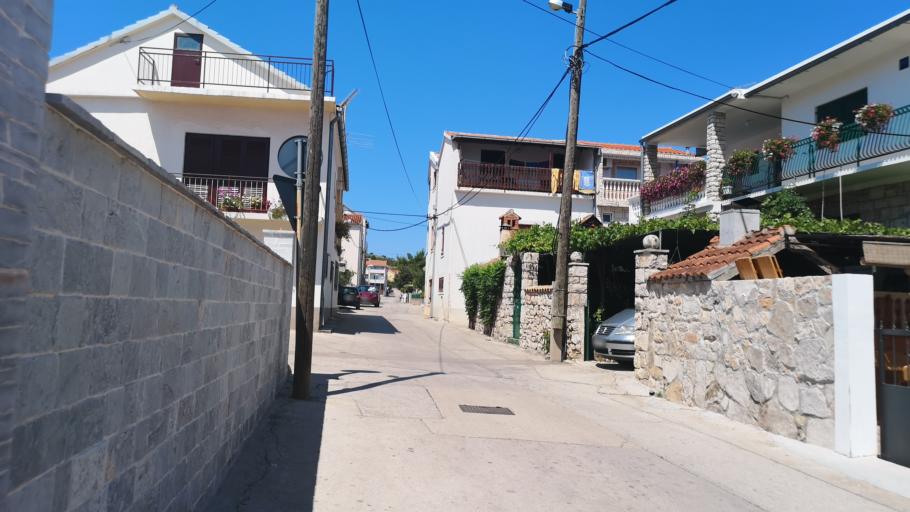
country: HR
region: Sibensko-Kniniska
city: Vodice
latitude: 43.7590
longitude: 15.7721
